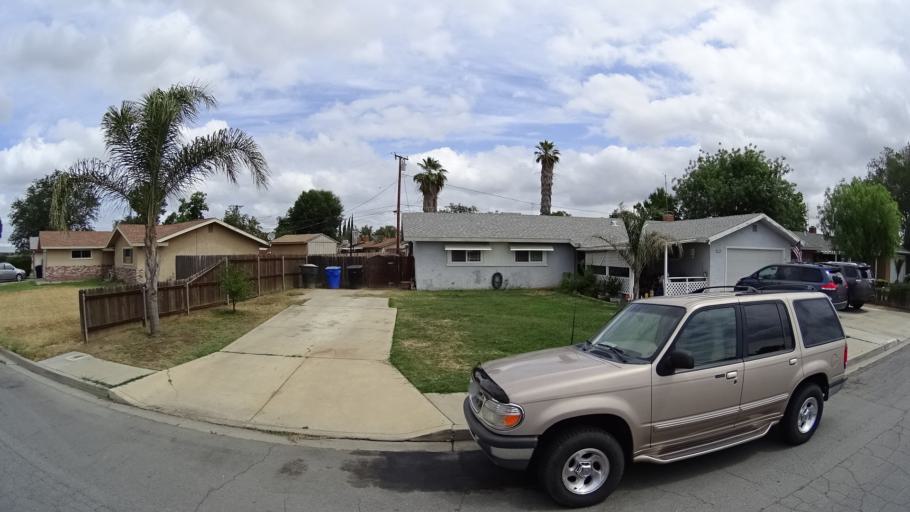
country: US
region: California
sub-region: Kings County
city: Home Garden
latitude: 36.3024
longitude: -119.6607
